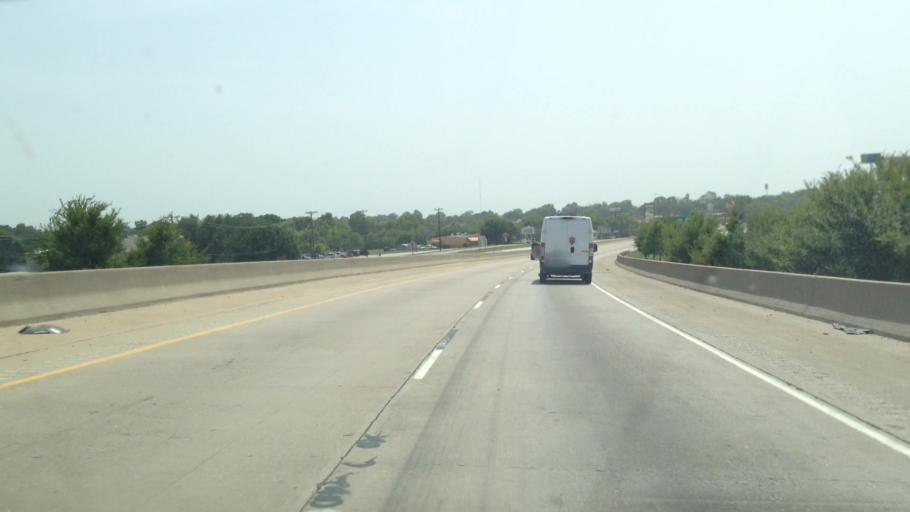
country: US
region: Texas
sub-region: Hopkins County
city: Sulphur Springs
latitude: 33.1193
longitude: -95.5864
